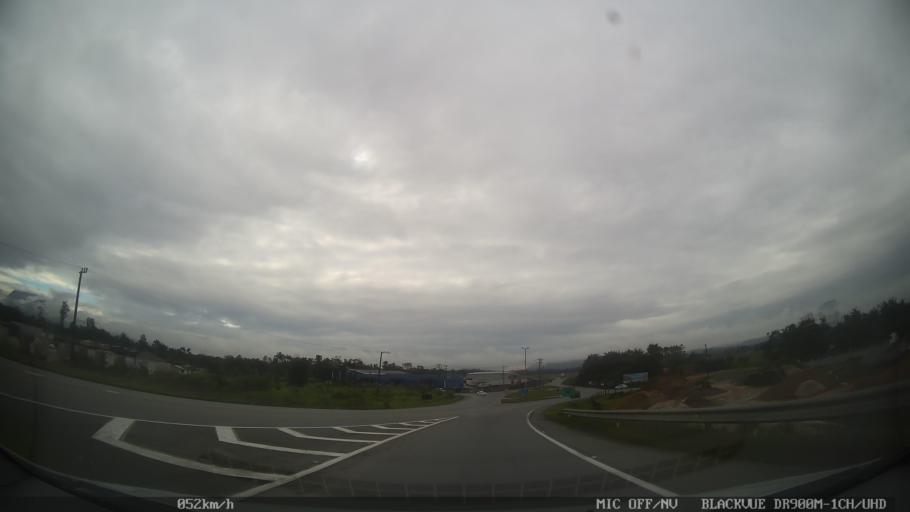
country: BR
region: Santa Catarina
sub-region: Joinville
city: Joinville
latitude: -26.0666
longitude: -48.8589
